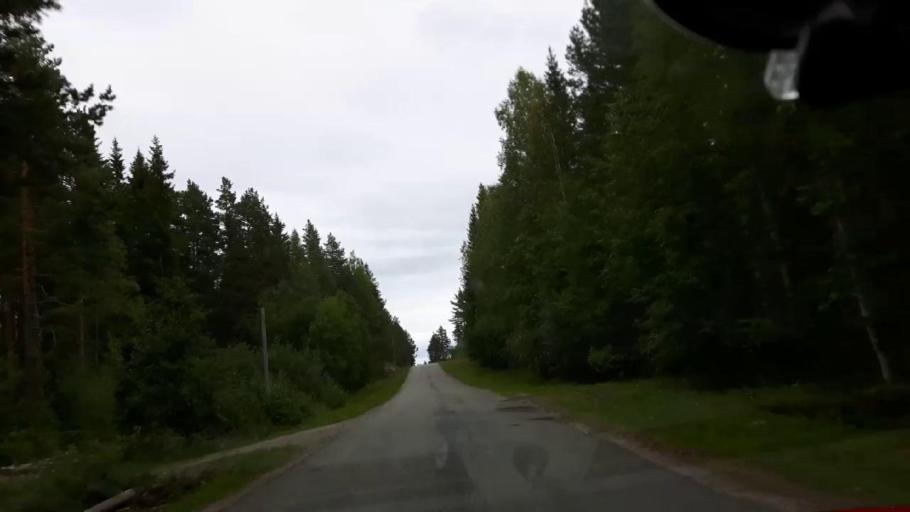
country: SE
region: Vaesternorrland
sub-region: Ange Kommun
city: Fransta
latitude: 62.7714
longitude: 16.0376
